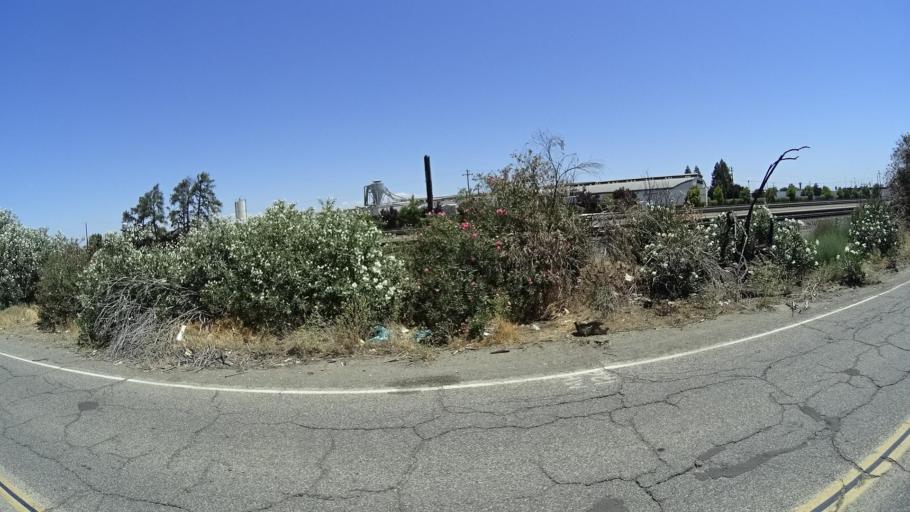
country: US
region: California
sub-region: Fresno County
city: Fresno
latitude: 36.7090
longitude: -119.7683
